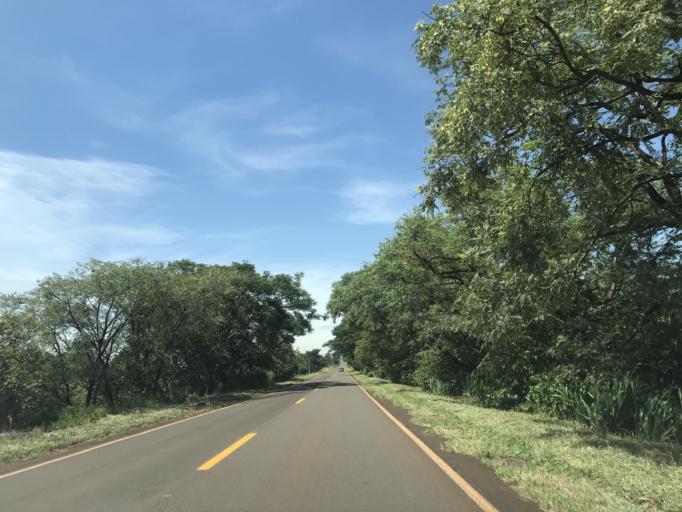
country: BR
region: Parana
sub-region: Paranavai
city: Nova Aurora
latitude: -22.8153
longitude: -52.6546
